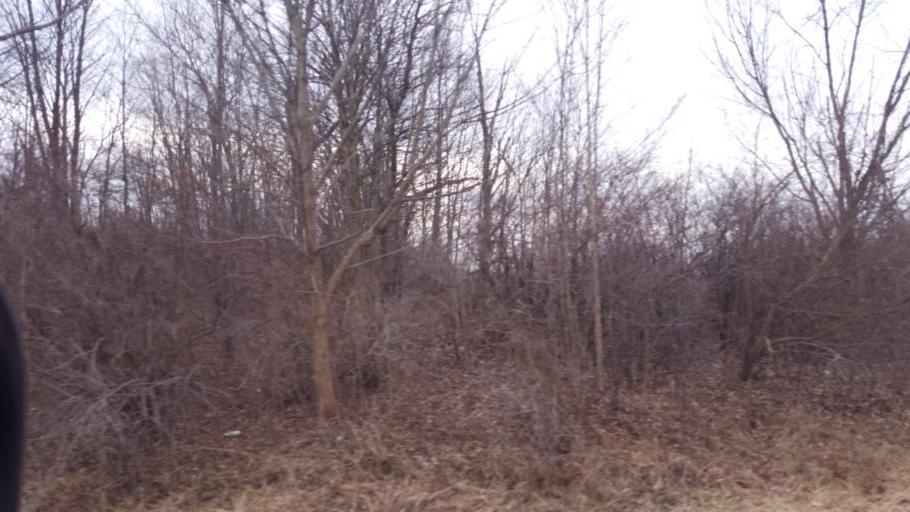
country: US
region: Ohio
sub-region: Richland County
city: Mansfield
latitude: 40.8059
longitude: -82.5351
